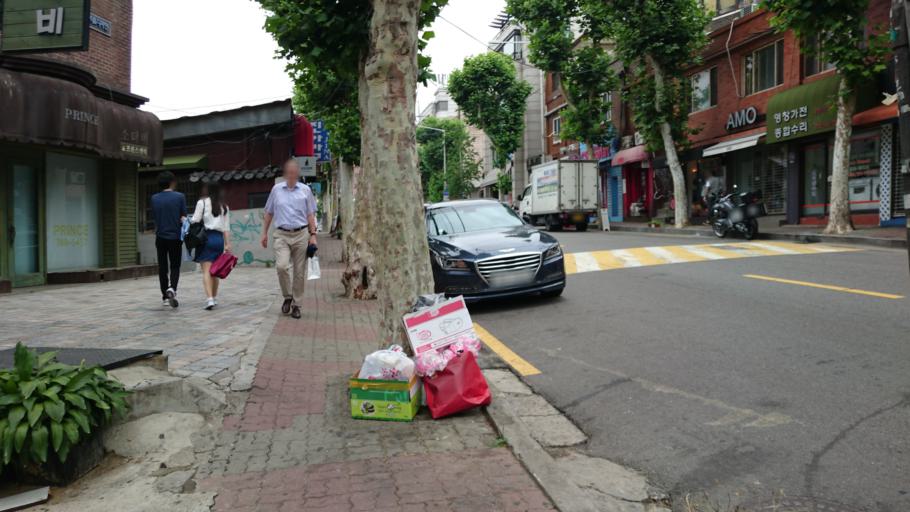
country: KR
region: Seoul
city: Seoul
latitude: 37.5324
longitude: 126.9946
